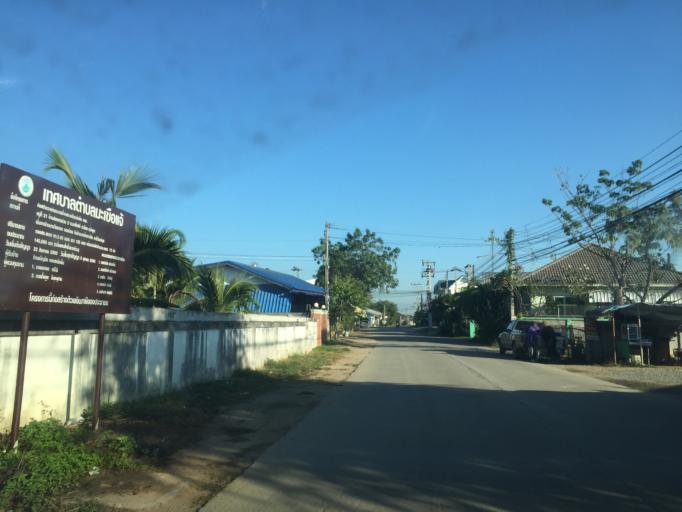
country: TH
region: Lamphun
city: Lamphun
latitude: 18.6097
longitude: 99.0565
